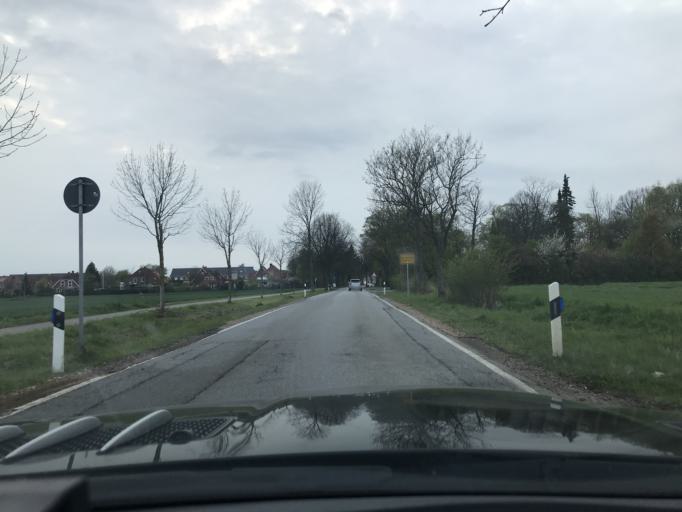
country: DE
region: Schleswig-Holstein
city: Burg auf Fehmarn
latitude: 54.4342
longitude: 11.2095
